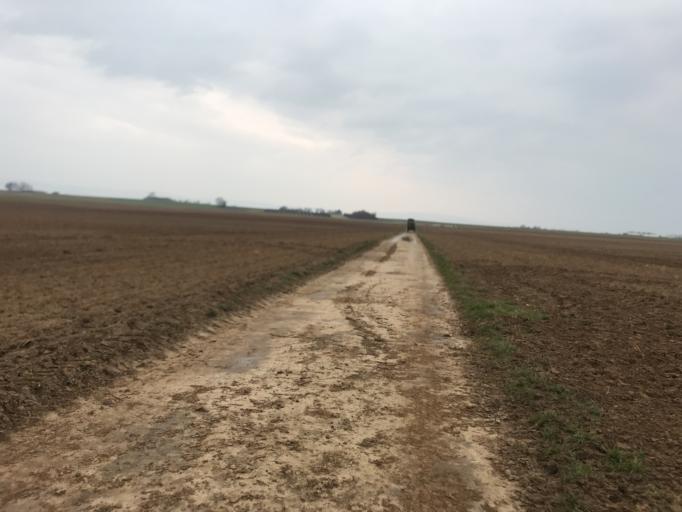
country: DE
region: Rheinland-Pfalz
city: Essenheim
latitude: 49.9473
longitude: 8.1399
